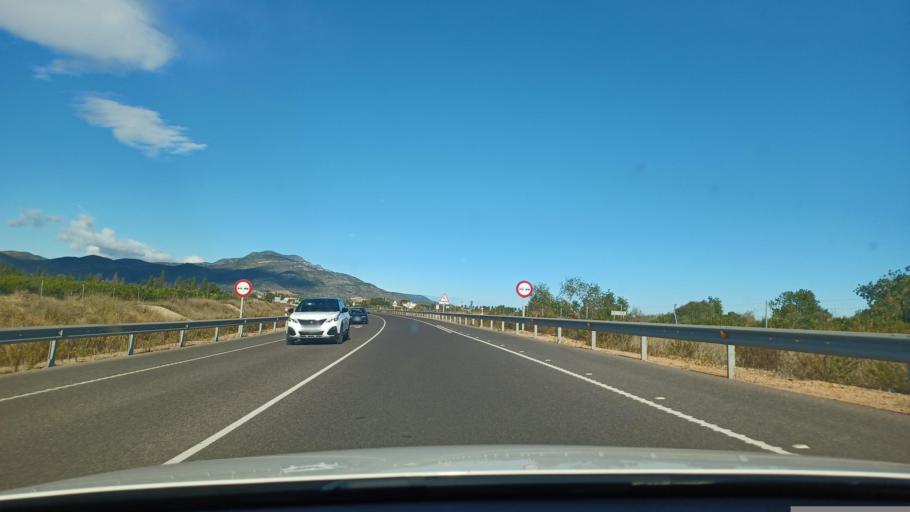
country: ES
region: Catalonia
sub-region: Provincia de Tarragona
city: Alcanar
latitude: 40.5215
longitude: 0.5046
